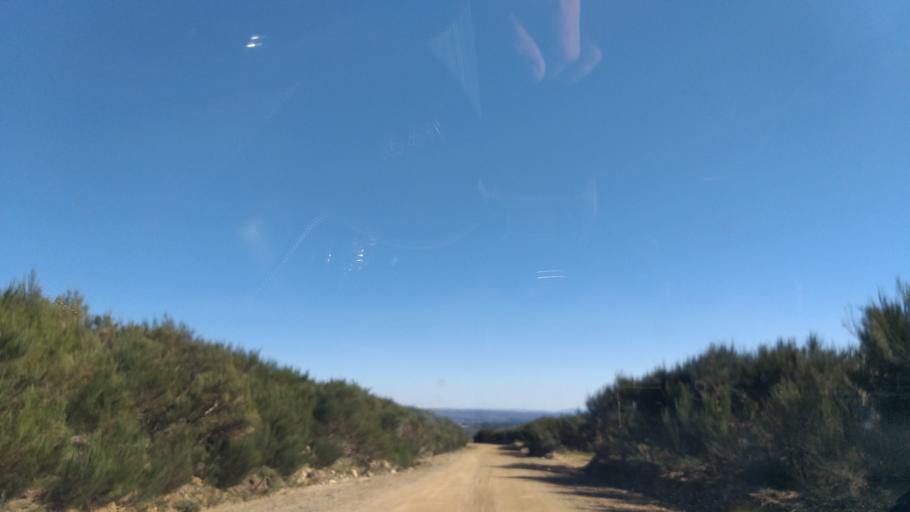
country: PT
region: Guarda
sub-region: Manteigas
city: Manteigas
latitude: 40.5056
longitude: -7.4772
